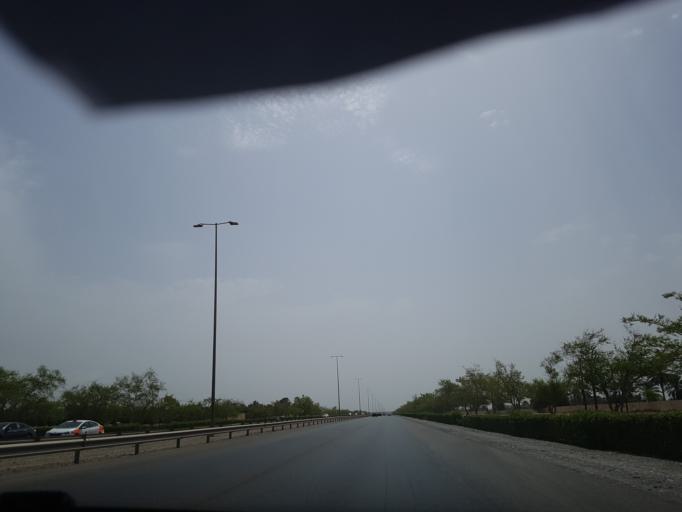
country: OM
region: Al Batinah
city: Barka'
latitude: 23.7320
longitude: 57.6940
